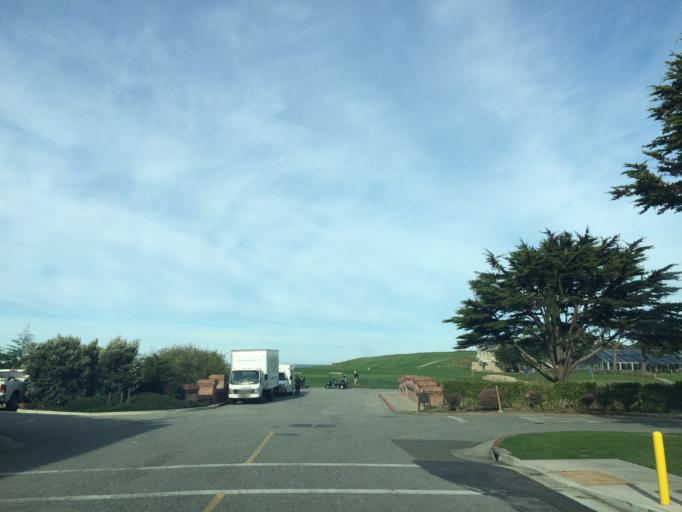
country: US
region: California
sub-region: San Mateo County
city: Half Moon Bay
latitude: 37.4347
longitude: -122.4405
